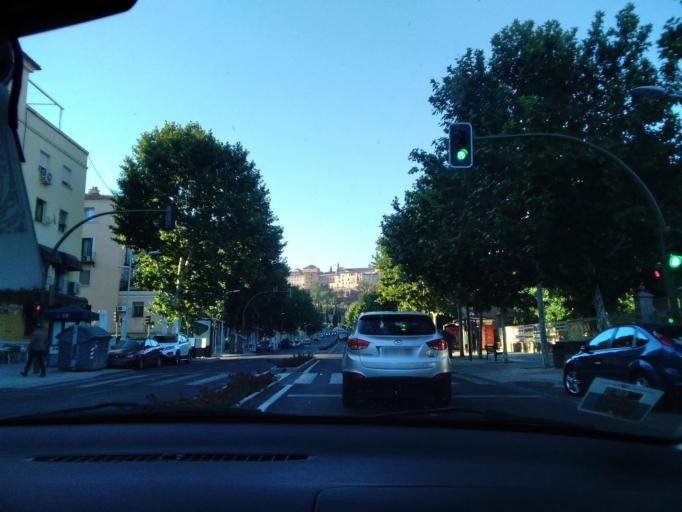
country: ES
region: Castille-La Mancha
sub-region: Province of Toledo
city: Toledo
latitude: 39.8657
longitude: -4.0286
